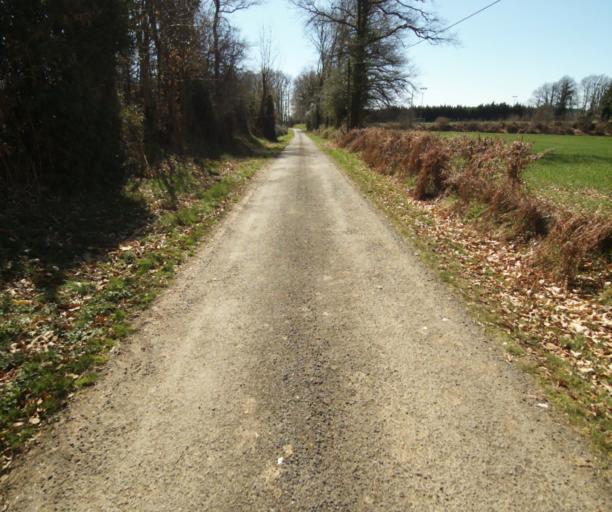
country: FR
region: Limousin
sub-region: Departement de la Correze
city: Saint-Clement
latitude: 45.3959
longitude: 1.6391
